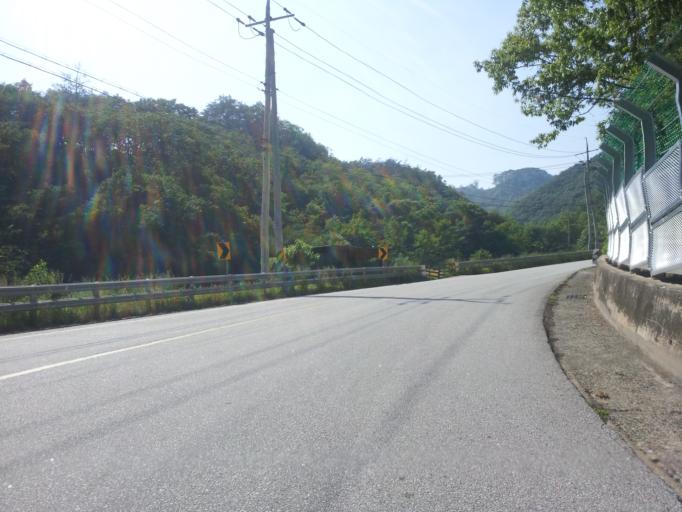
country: KR
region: Chungcheongbuk-do
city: Okcheon
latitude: 36.4790
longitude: 127.6539
